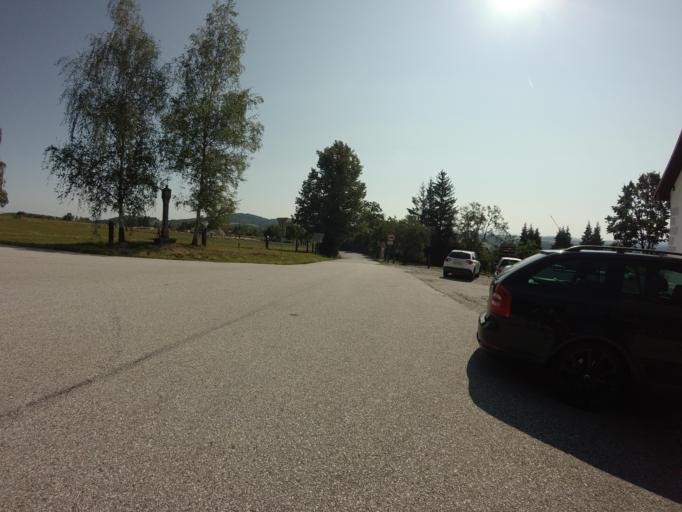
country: CZ
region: Jihocesky
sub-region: Okres Cesky Krumlov
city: Cesky Krumlov
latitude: 48.8511
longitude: 14.3504
